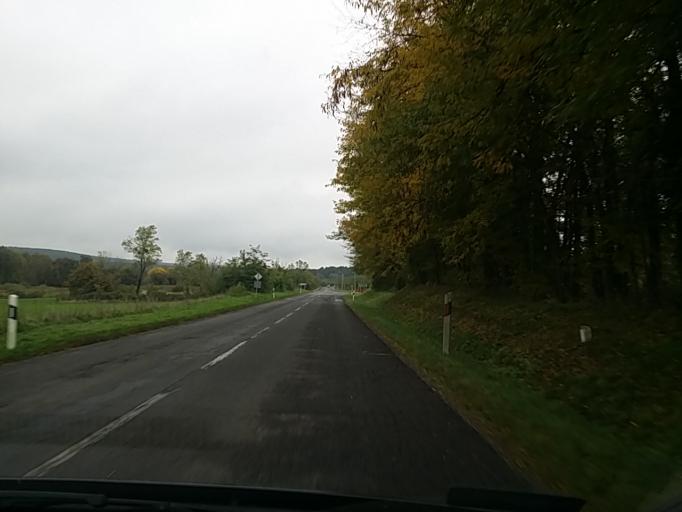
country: HU
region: Somogy
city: Karad
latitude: 46.6249
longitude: 17.7947
